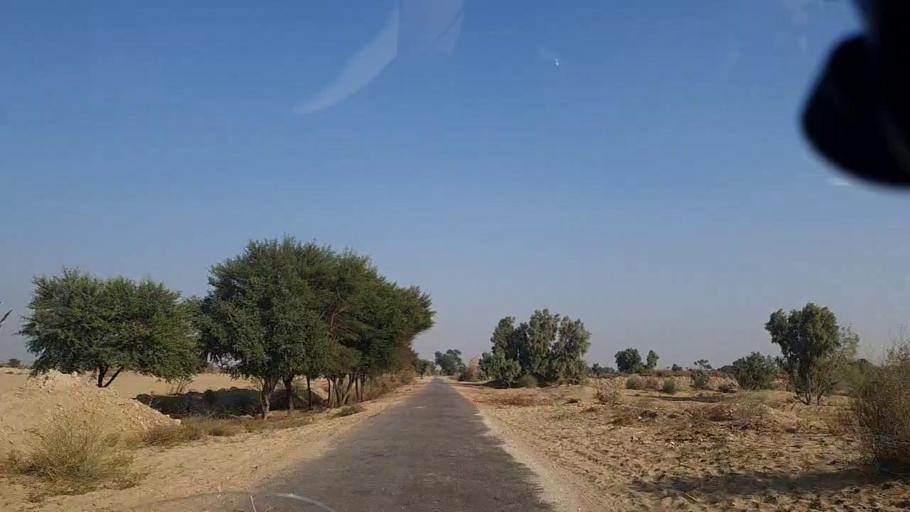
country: PK
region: Sindh
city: Khanpur
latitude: 27.6878
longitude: 69.5118
